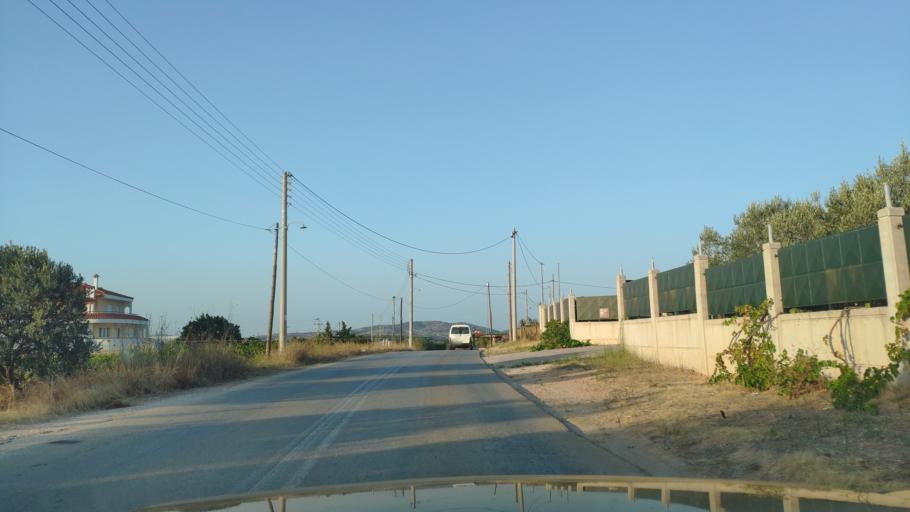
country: GR
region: Attica
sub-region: Nomarchia Anatolikis Attikis
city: Markopoulo
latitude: 37.9046
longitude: 23.9606
